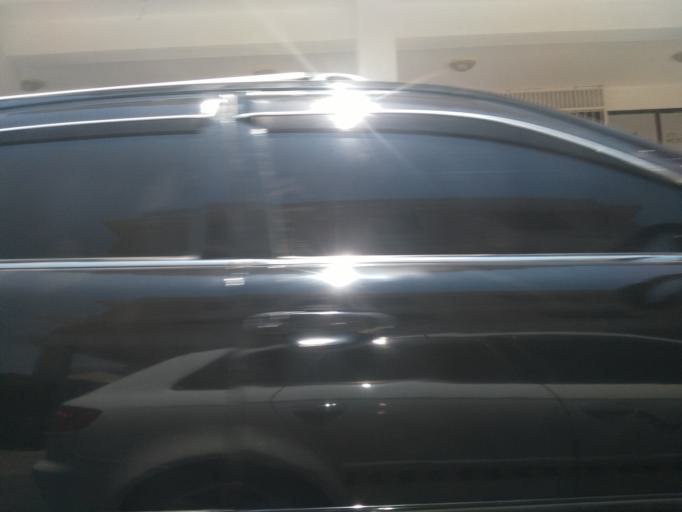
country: TZ
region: Dodoma
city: Dodoma
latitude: -6.1803
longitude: 35.7451
